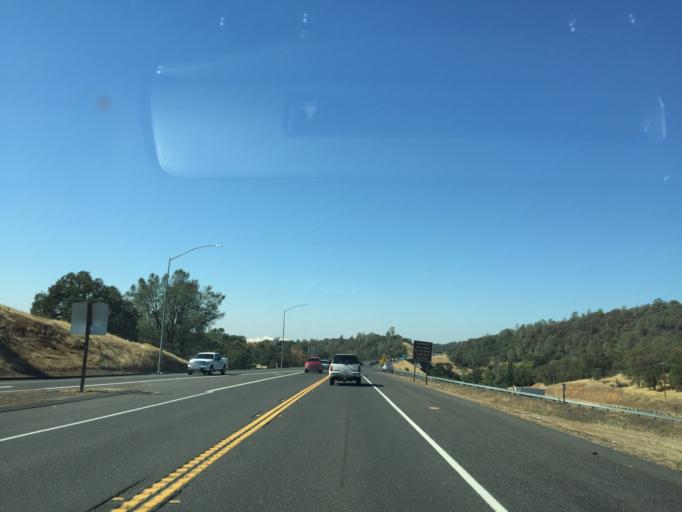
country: US
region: California
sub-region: Tuolumne County
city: East Sonora
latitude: 37.9794
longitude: -120.3392
